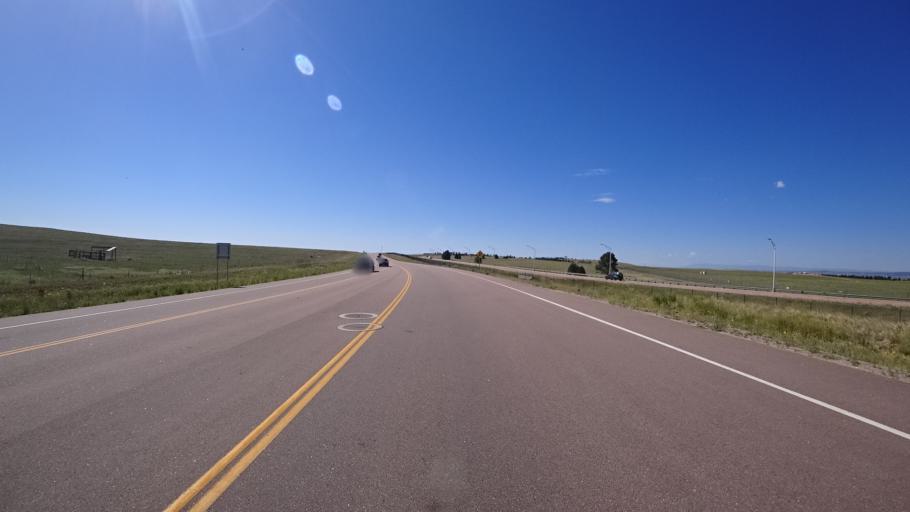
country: US
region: Colorado
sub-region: El Paso County
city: Cimarron Hills
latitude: 38.8241
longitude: -104.6824
